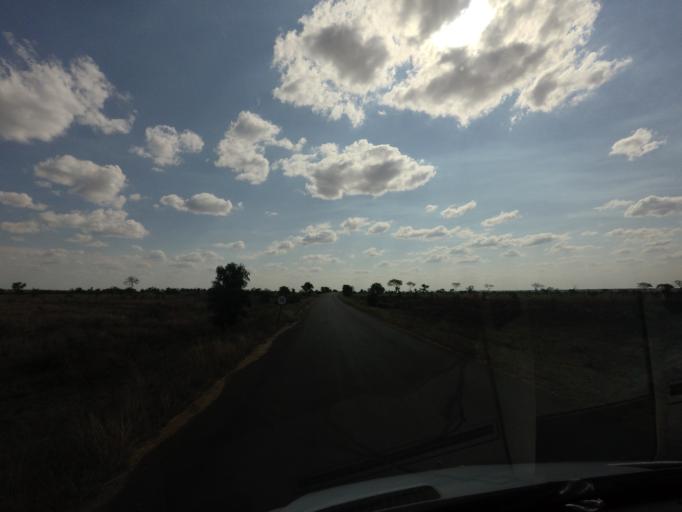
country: ZA
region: Limpopo
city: Thulamahashi
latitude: -24.3914
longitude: 31.6067
